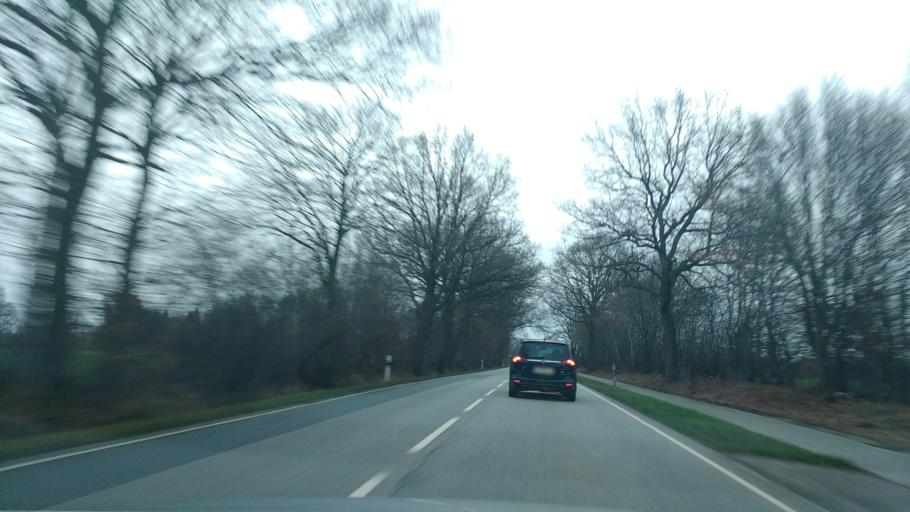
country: DE
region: Schleswig-Holstein
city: Oelixdorf
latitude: 53.9546
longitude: 9.5569
